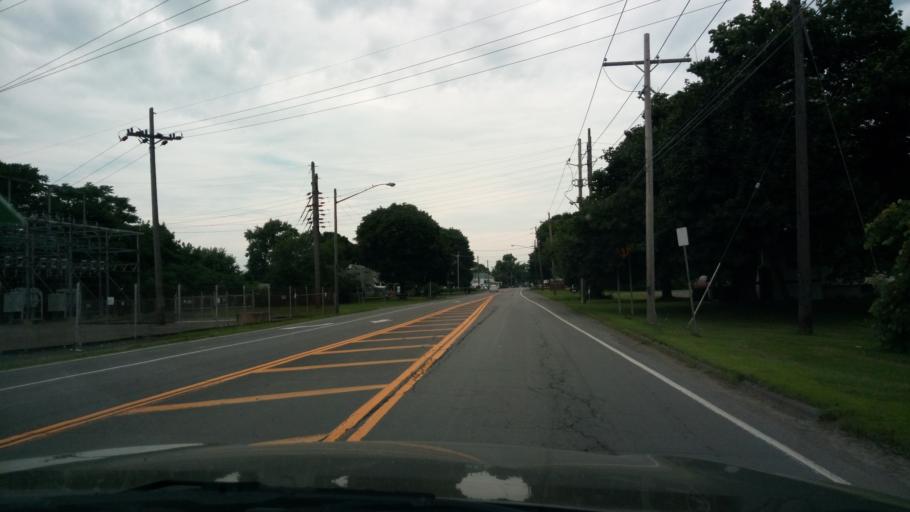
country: US
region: New York
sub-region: Chemung County
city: Elmira Heights
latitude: 42.1312
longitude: -76.8114
